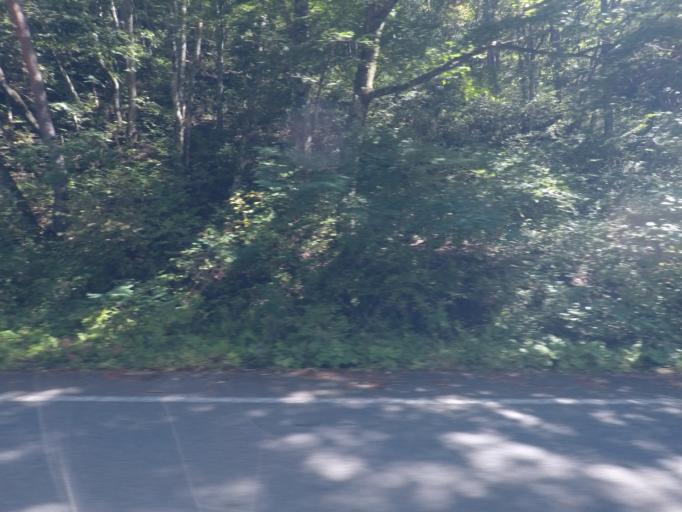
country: JP
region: Nagano
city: Shiojiri
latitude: 35.9964
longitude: 137.7389
